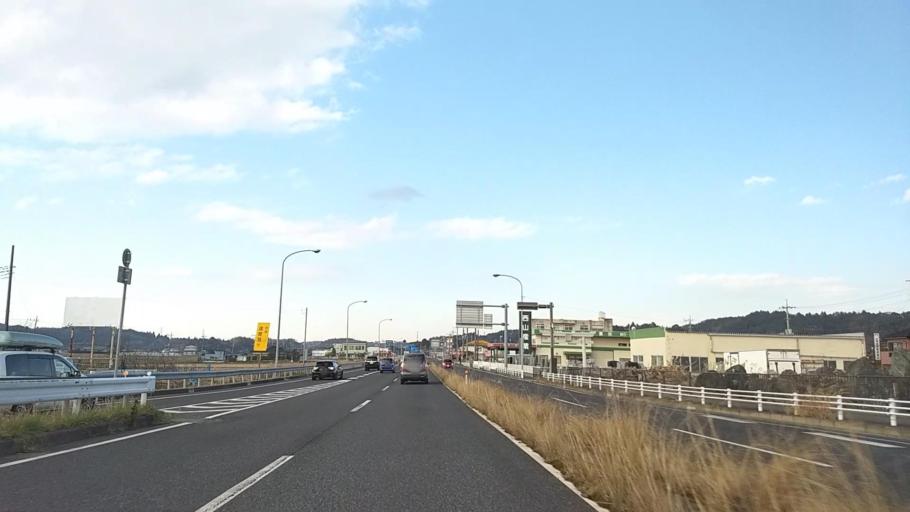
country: JP
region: Chiba
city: Togane
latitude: 35.5531
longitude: 140.3478
